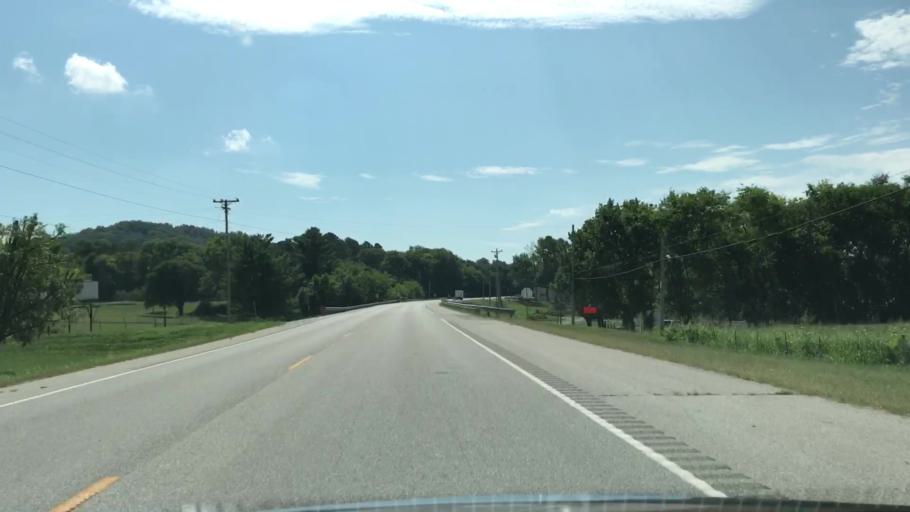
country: US
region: Tennessee
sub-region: Smith County
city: Carthage
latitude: 36.3339
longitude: -86.0257
